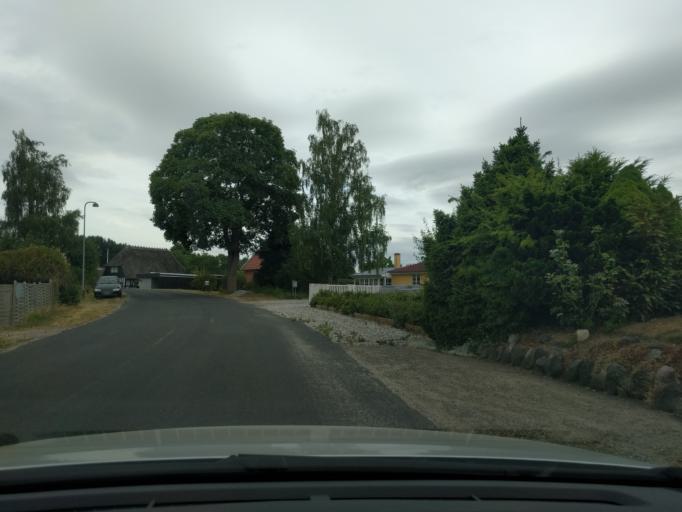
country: DK
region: South Denmark
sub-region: Odense Kommune
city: Odense
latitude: 55.4194
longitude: 10.3711
